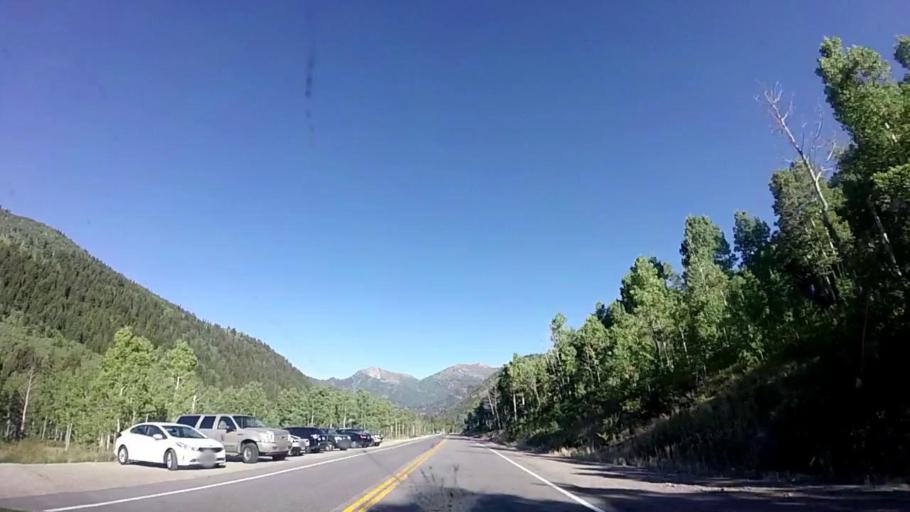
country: US
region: Utah
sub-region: Summit County
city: Snyderville
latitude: 40.6336
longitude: -111.6118
